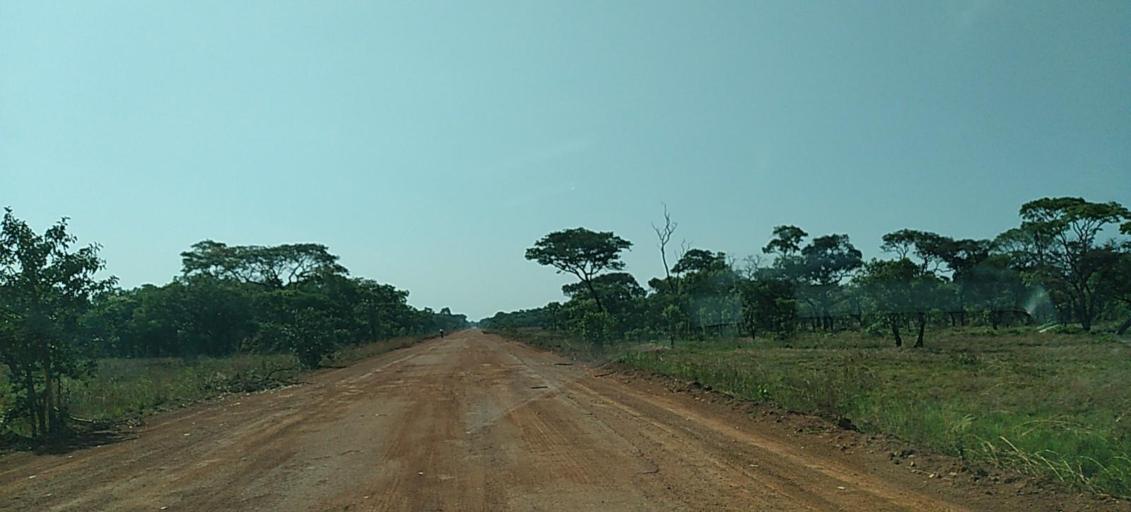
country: ZM
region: North-Western
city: Mwinilunga
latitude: -11.9109
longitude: 25.2981
